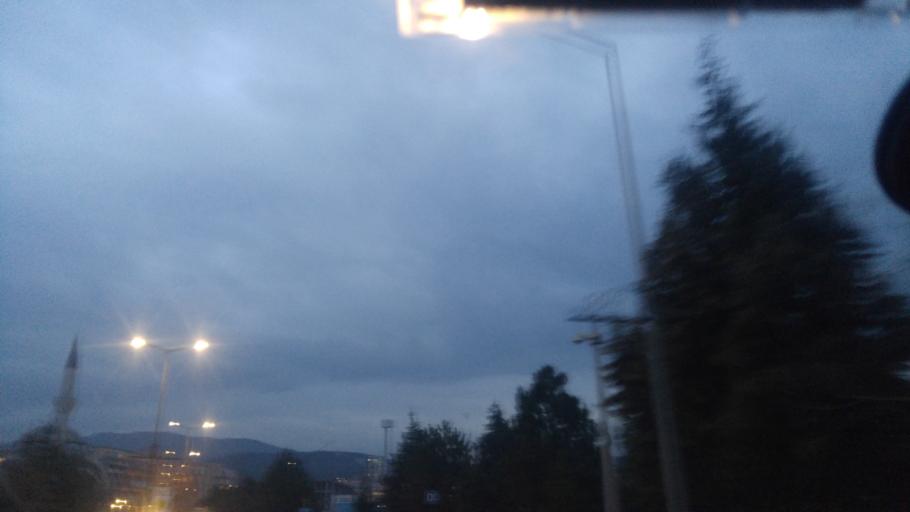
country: TR
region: Karabuk
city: Karabuk
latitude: 41.2129
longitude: 32.6525
